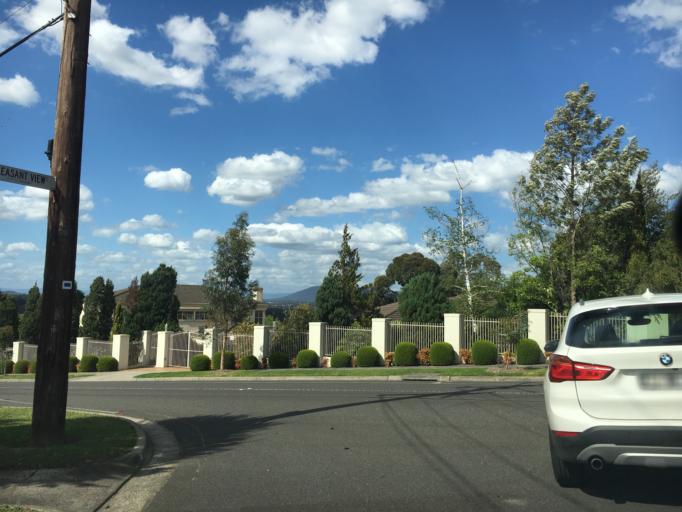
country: AU
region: Victoria
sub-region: Monash
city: Mulgrave
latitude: -37.8928
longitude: 145.1820
